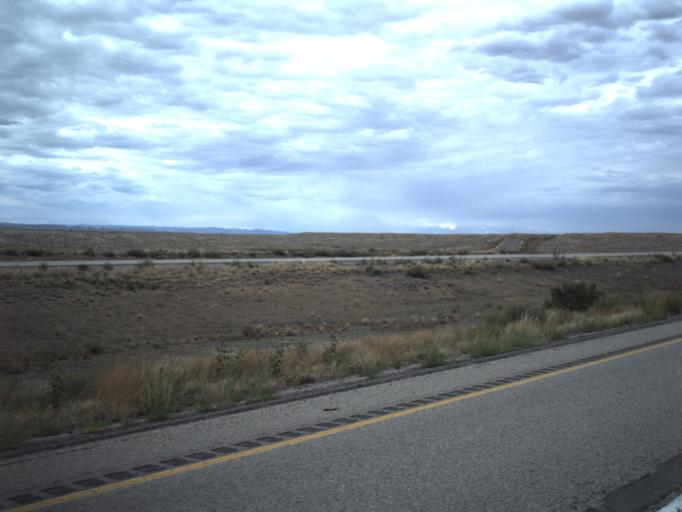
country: US
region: Utah
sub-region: Grand County
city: Moab
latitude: 38.9353
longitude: -109.4143
